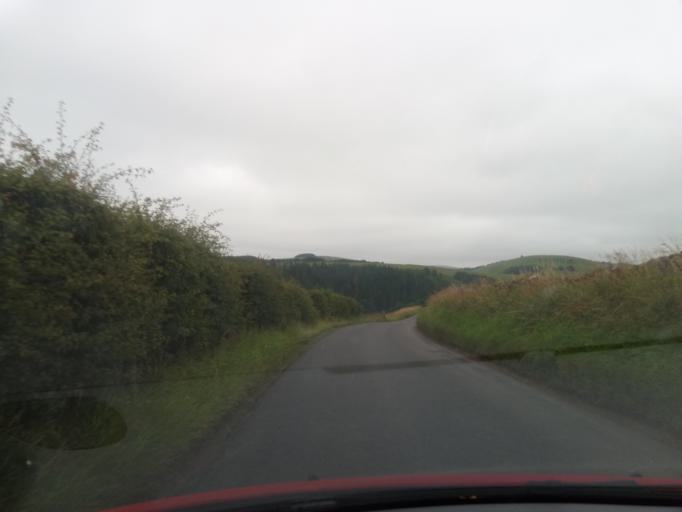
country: GB
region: Scotland
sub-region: Fife
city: Pathhead
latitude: 55.7717
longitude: -2.9516
